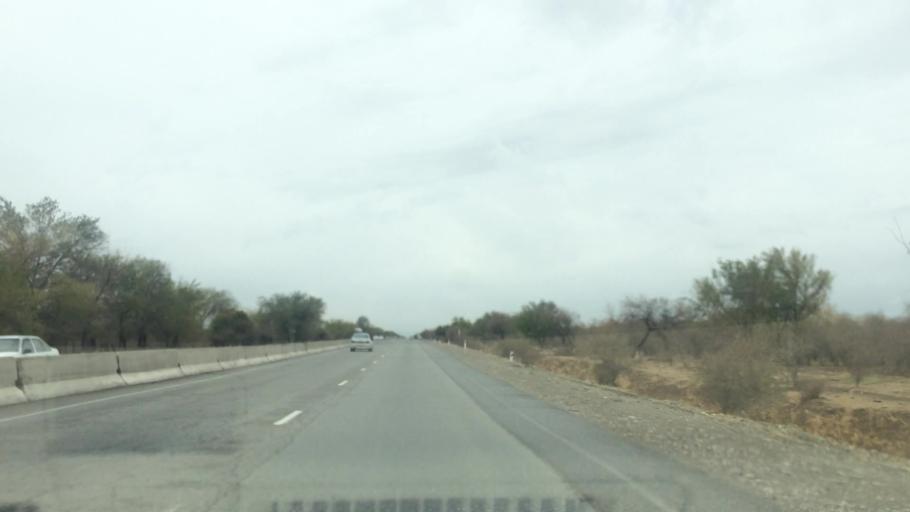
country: UZ
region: Samarqand
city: Bulung'ur
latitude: 39.8197
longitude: 67.3870
